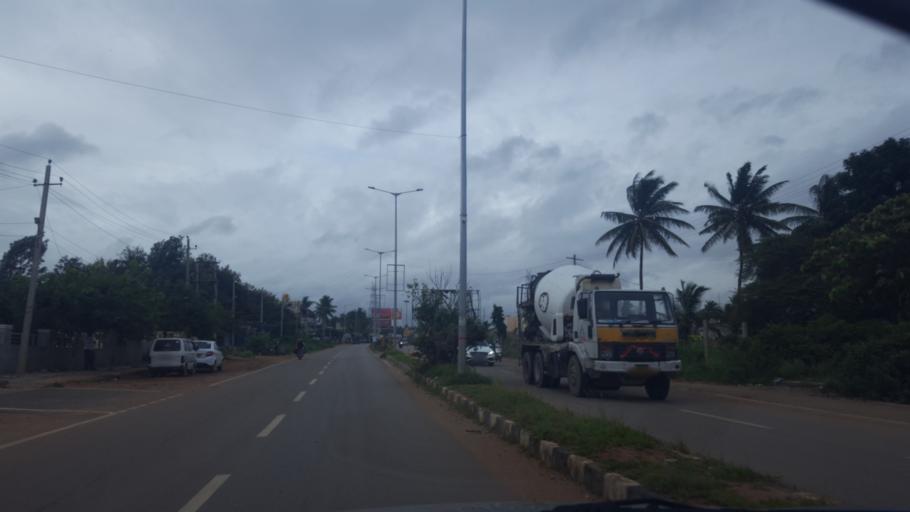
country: IN
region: Karnataka
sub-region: Bangalore Urban
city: Yelahanka
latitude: 13.1398
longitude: 77.6707
